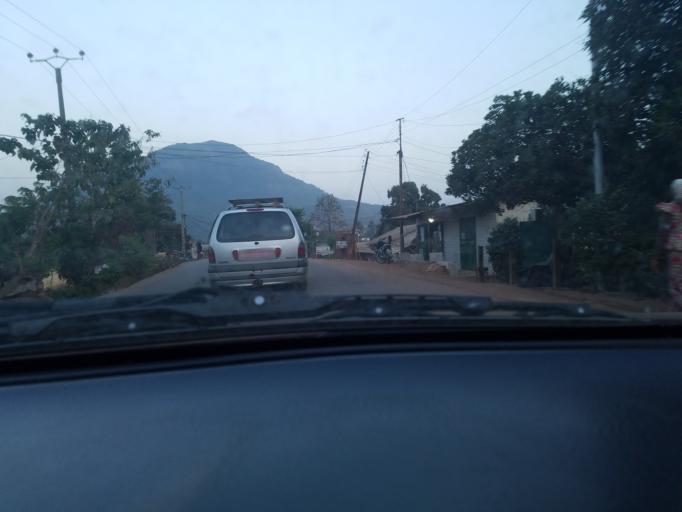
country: GN
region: Kindia
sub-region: Prefecture de Dubreka
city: Dubreka
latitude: 9.7879
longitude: -13.4883
